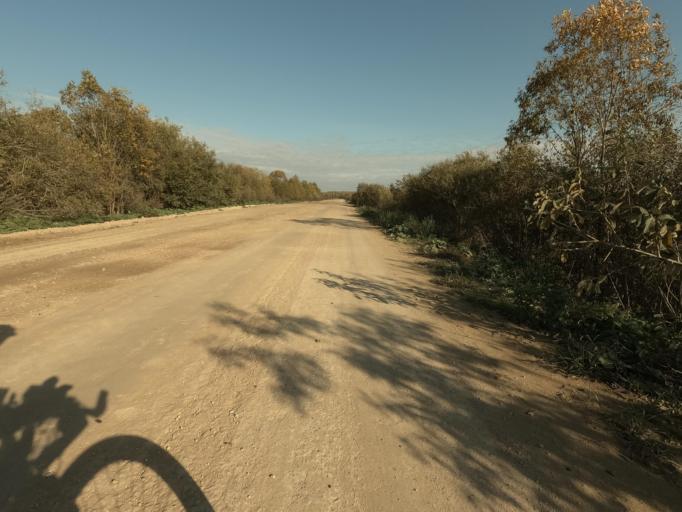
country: RU
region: Novgorod
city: Batetskiy
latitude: 58.8158
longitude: 30.6990
